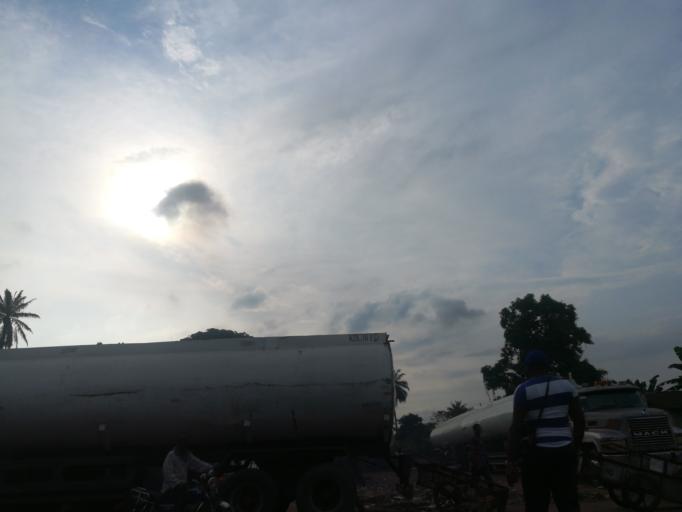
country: NG
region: Rivers
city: Okrika
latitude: 4.7734
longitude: 7.1064
